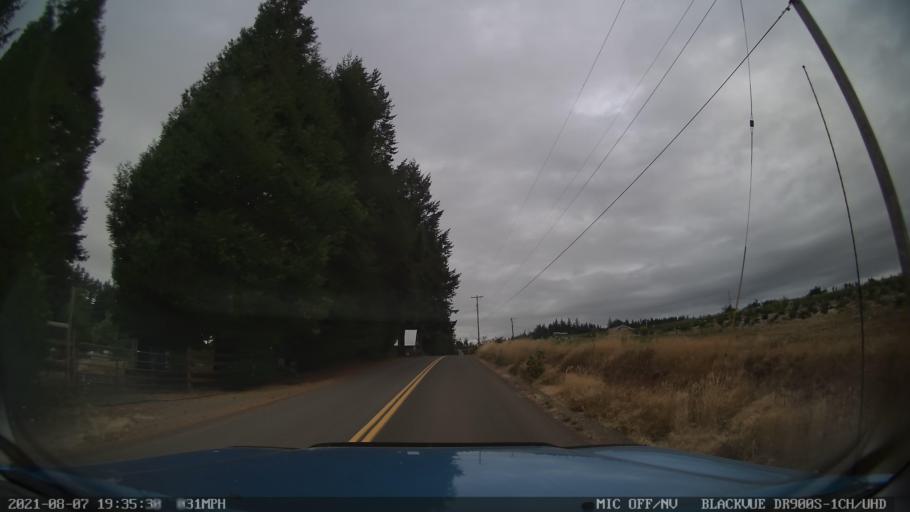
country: US
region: Oregon
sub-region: Marion County
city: Silverton
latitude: 44.9271
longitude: -122.6567
